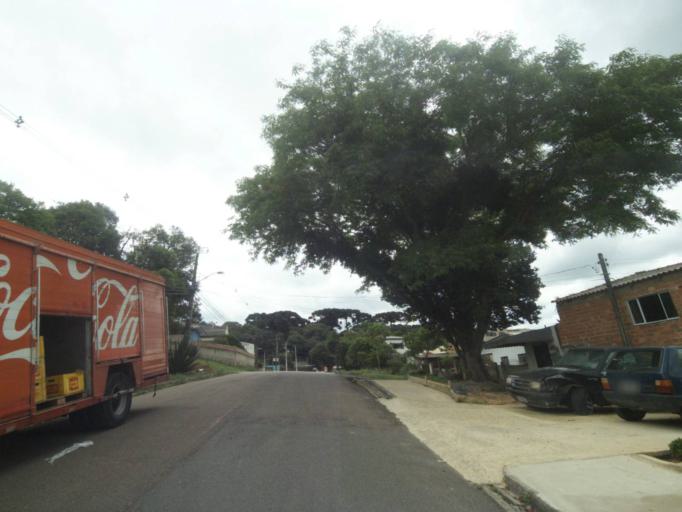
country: BR
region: Parana
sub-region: Curitiba
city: Curitiba
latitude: -25.3884
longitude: -49.2880
